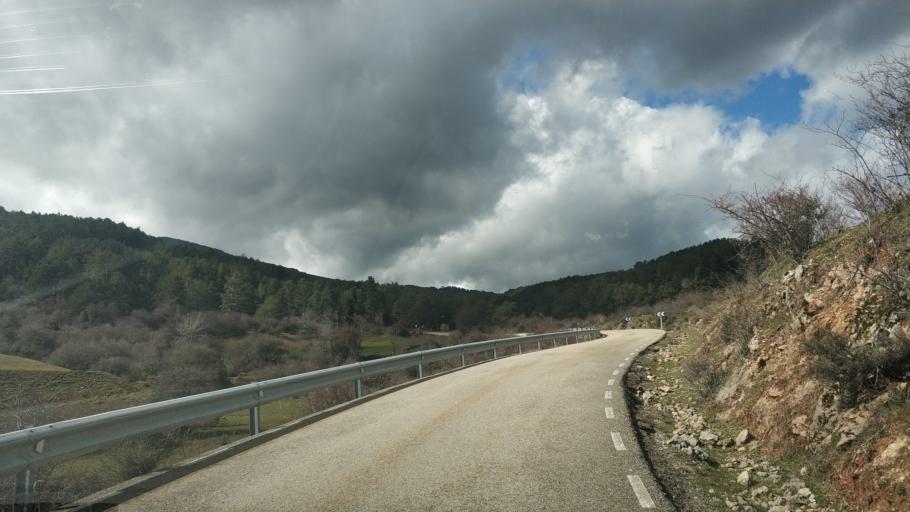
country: ES
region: Castille and Leon
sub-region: Provincia de Burgos
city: Neila
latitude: 42.0566
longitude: -3.0086
